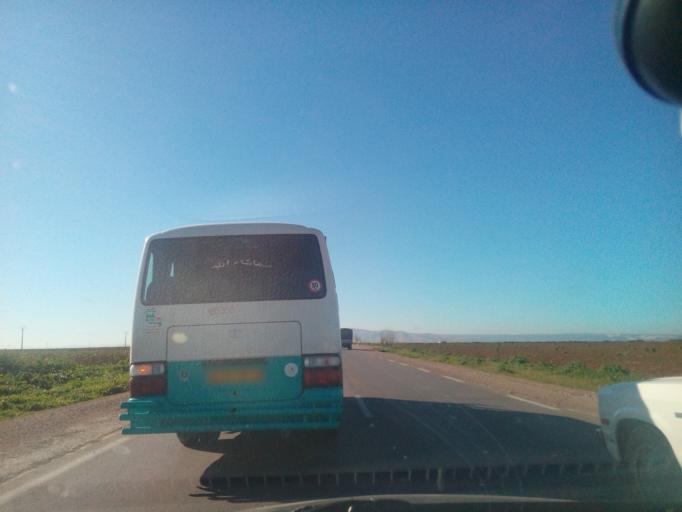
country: DZ
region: Relizane
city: Relizane
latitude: 35.8927
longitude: 0.6343
